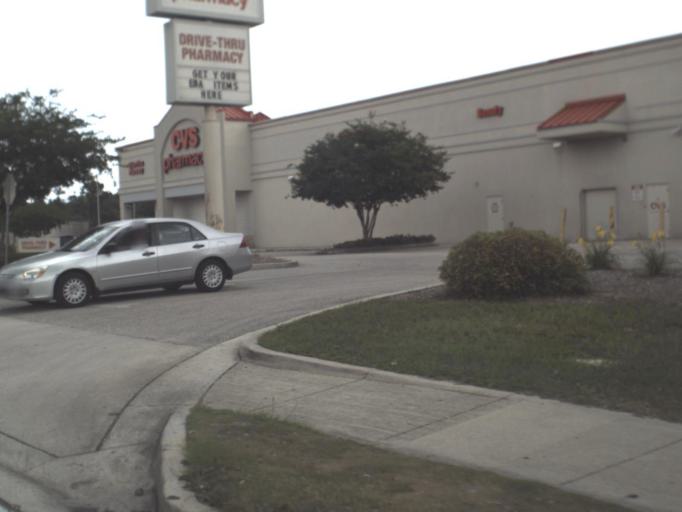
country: US
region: Florida
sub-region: Duval County
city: Jacksonville
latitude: 30.3155
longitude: -81.5606
